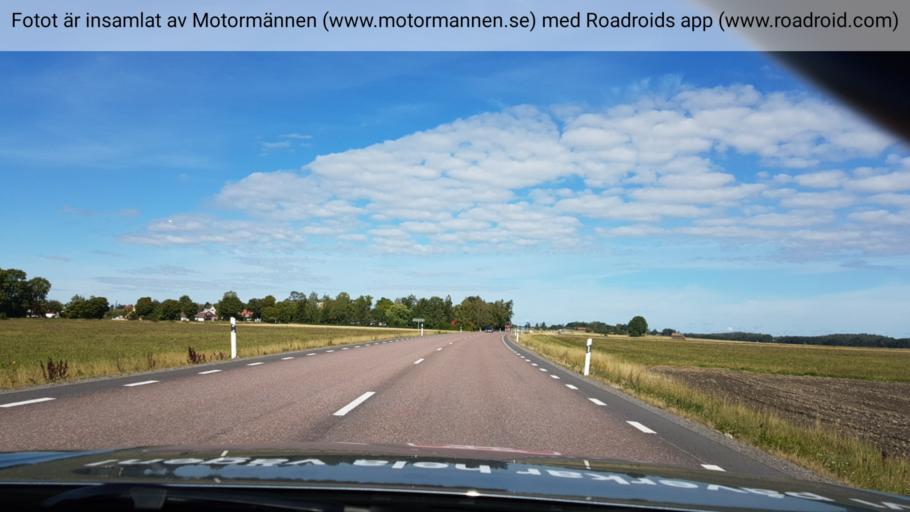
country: SE
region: Uppsala
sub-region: Osthammars Kommun
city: Bjorklinge
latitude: 59.9209
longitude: 17.5033
